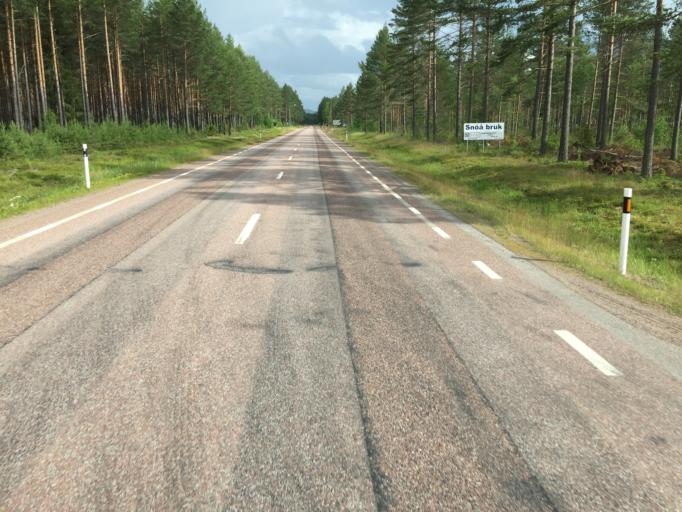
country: SE
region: Dalarna
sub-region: Vansbro Kommun
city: Jarna
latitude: 60.5372
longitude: 14.4244
